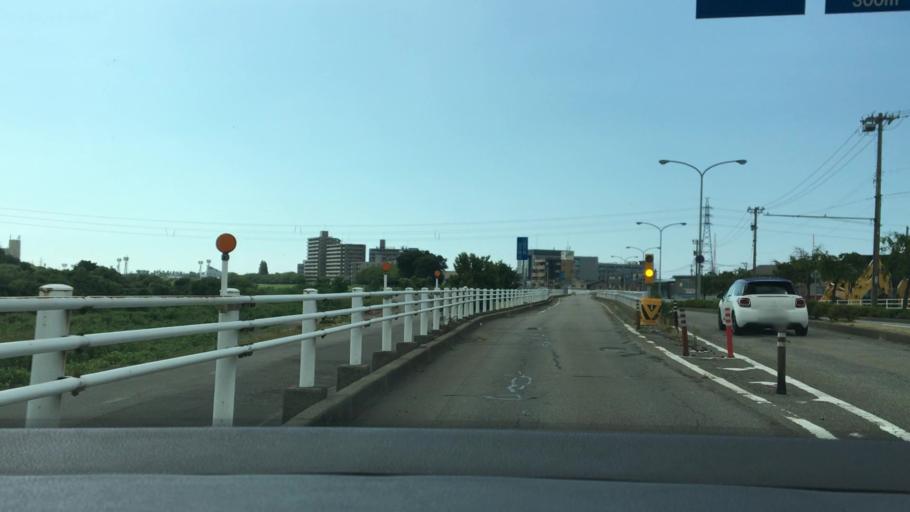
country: JP
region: Ishikawa
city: Kanazawa-shi
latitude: 36.5744
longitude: 136.6276
